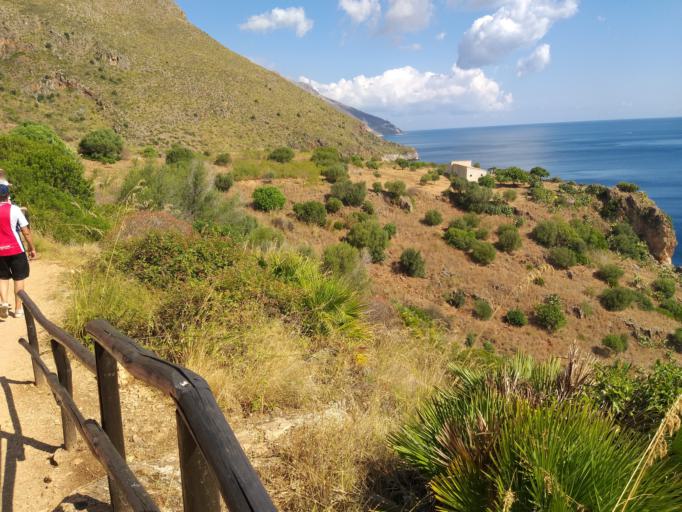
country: IT
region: Sicily
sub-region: Trapani
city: Castelluzzo
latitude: 38.0848
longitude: 12.8073
